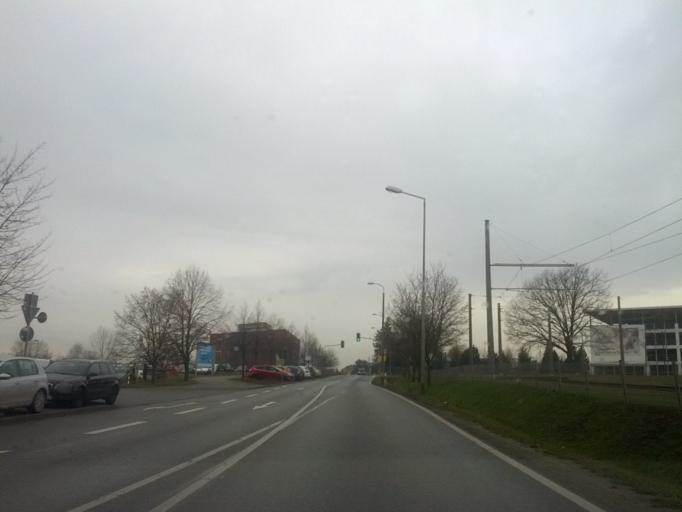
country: DE
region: Thuringia
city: Ingersleben
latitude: 50.9735
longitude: 10.9608
